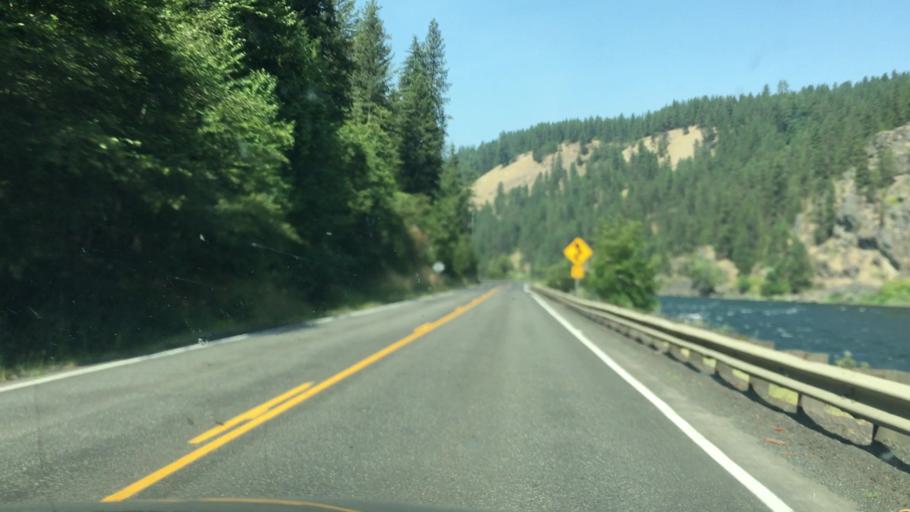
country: US
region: Idaho
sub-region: Clearwater County
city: Orofino
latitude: 46.4995
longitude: -116.3843
